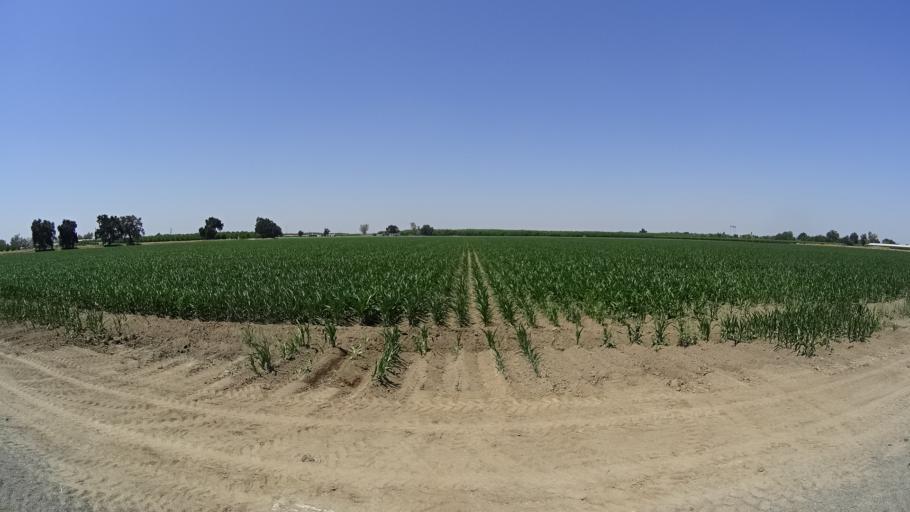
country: US
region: California
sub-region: Fresno County
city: Laton
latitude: 36.4176
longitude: -119.6865
